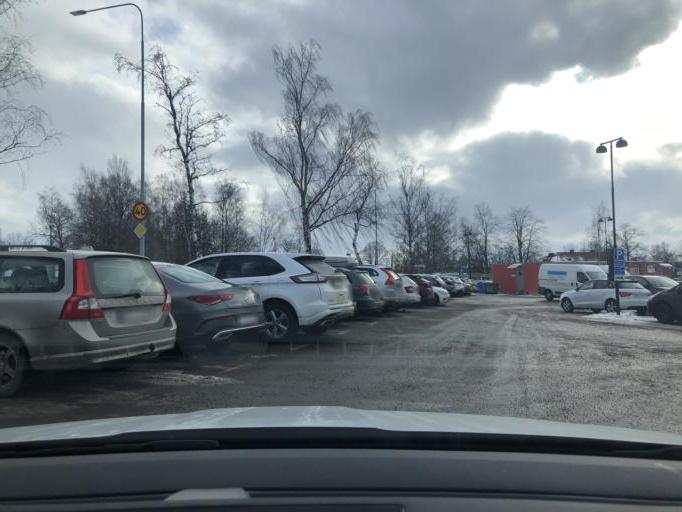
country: SE
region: OEstergoetland
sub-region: Motala Kommun
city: Motala
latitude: 58.5458
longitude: 15.0285
